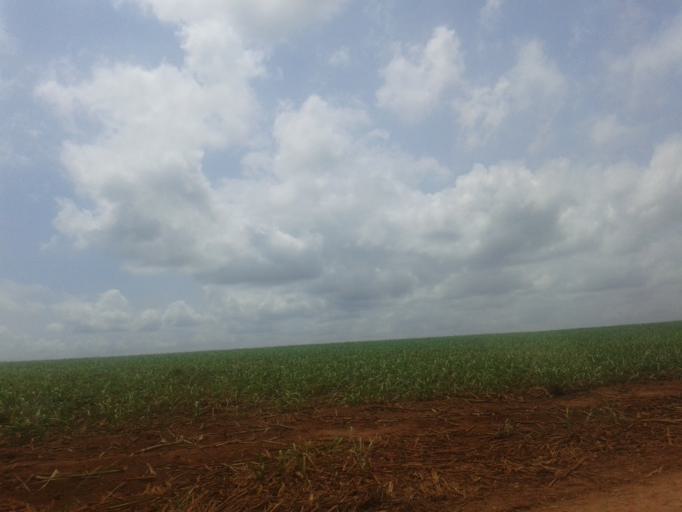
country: CM
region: Centre
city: Mbandjok
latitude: 4.4474
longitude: 11.9322
